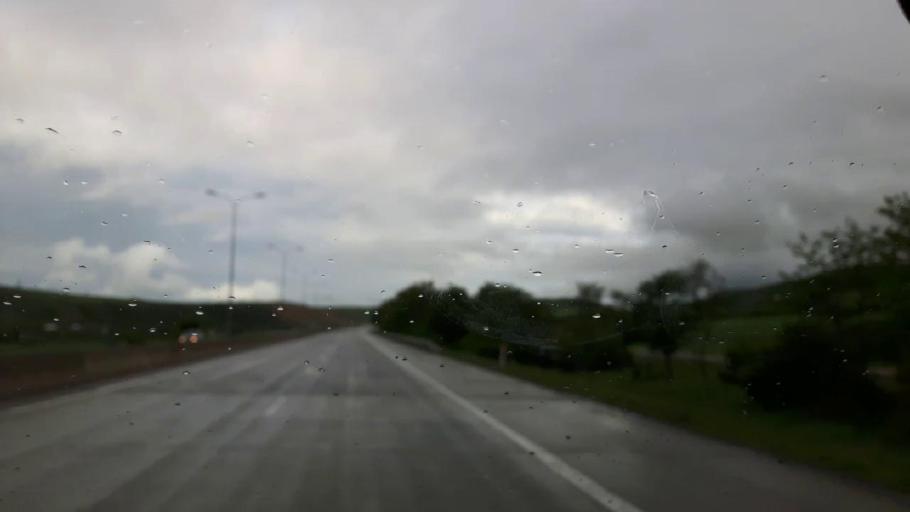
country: GE
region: Shida Kartli
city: Kaspi
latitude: 42.0012
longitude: 44.3819
